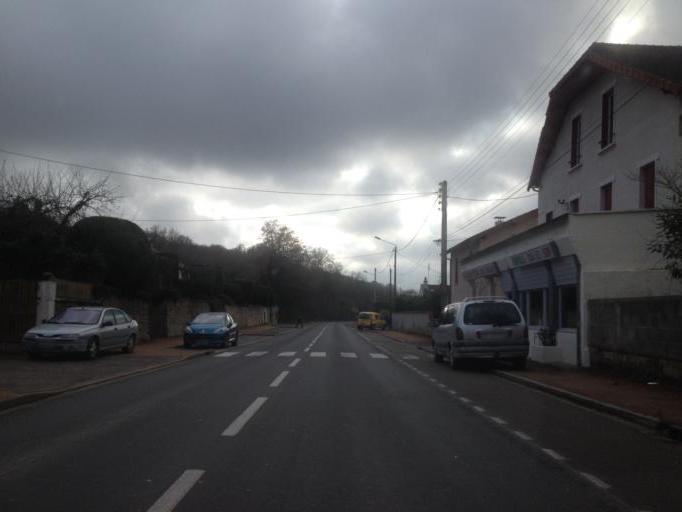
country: FR
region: Auvergne
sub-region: Departement de l'Allier
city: Creuzier-le-Vieux
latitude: 46.1529
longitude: 3.4120
